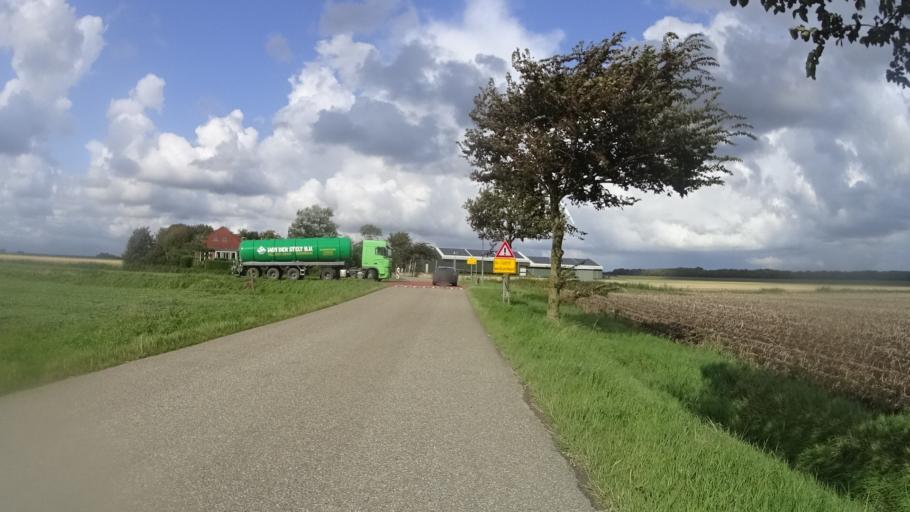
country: NL
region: North Holland
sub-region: Gemeente Schagen
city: Schagen
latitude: 52.8596
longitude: 4.8926
